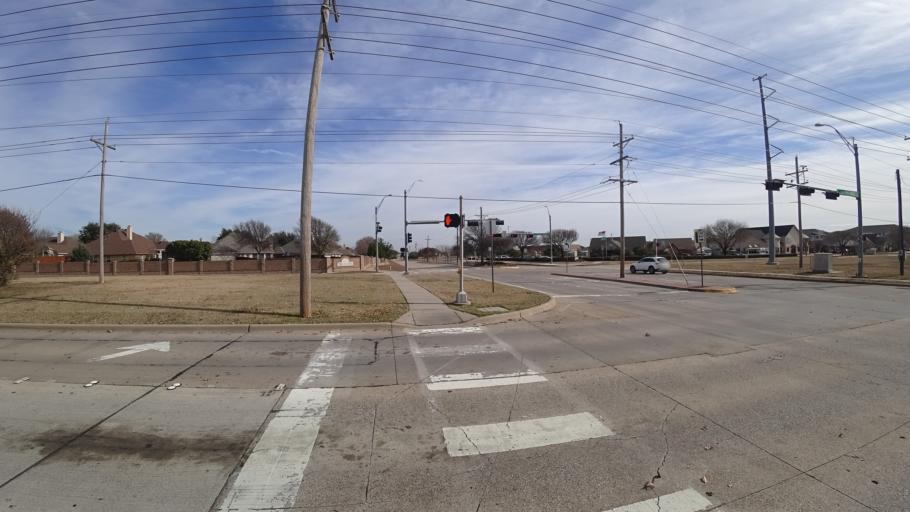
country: US
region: Texas
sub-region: Denton County
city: Highland Village
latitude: 33.0570
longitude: -97.0359
